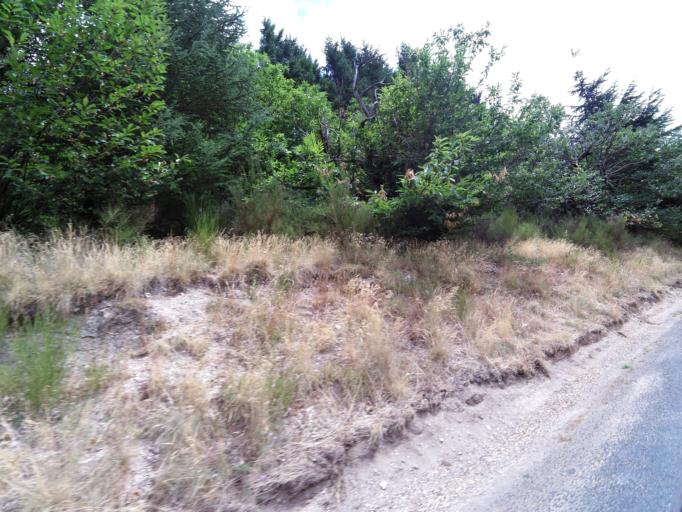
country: FR
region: Languedoc-Roussillon
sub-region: Departement du Gard
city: Le Vigan
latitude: 44.0211
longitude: 3.6285
